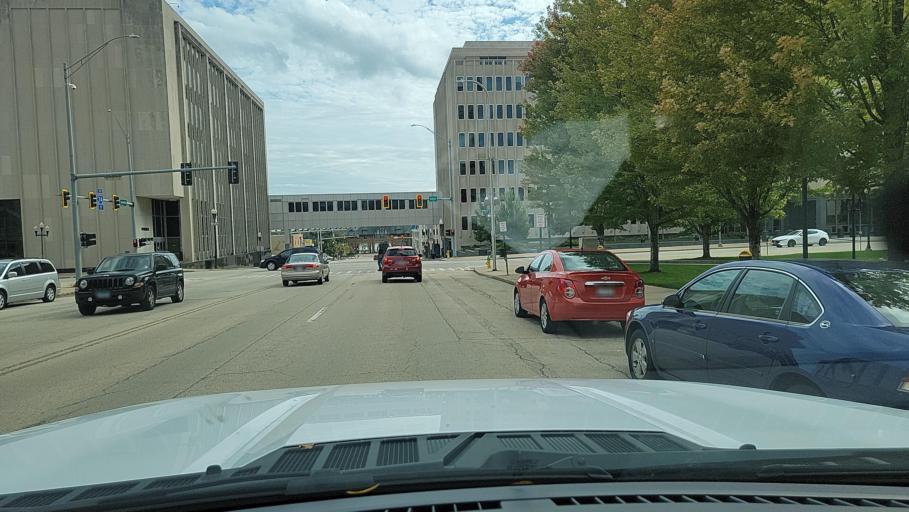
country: US
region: Illinois
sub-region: Peoria County
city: Peoria
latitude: 40.6929
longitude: -89.5887
